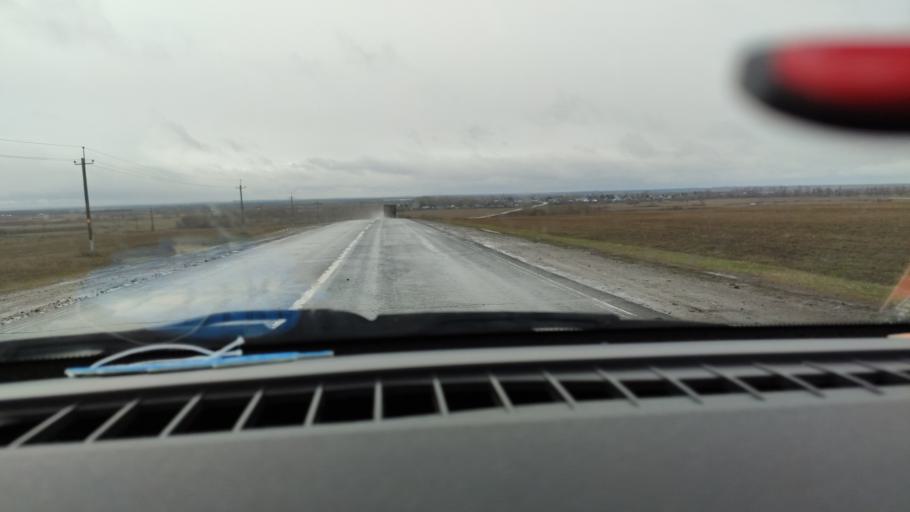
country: RU
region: Tatarstan
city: Nurlat
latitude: 54.5814
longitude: 50.8608
